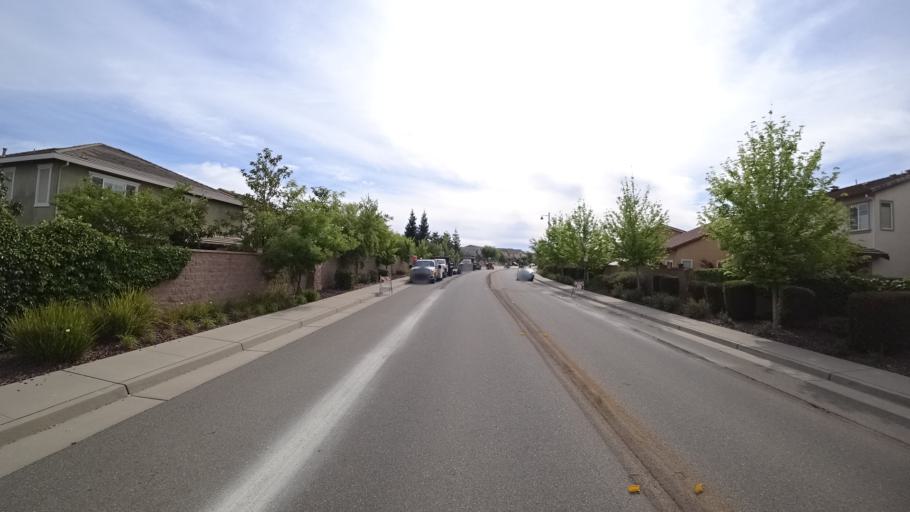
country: US
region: California
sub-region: Placer County
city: Lincoln
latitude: 38.8372
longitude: -121.2813
